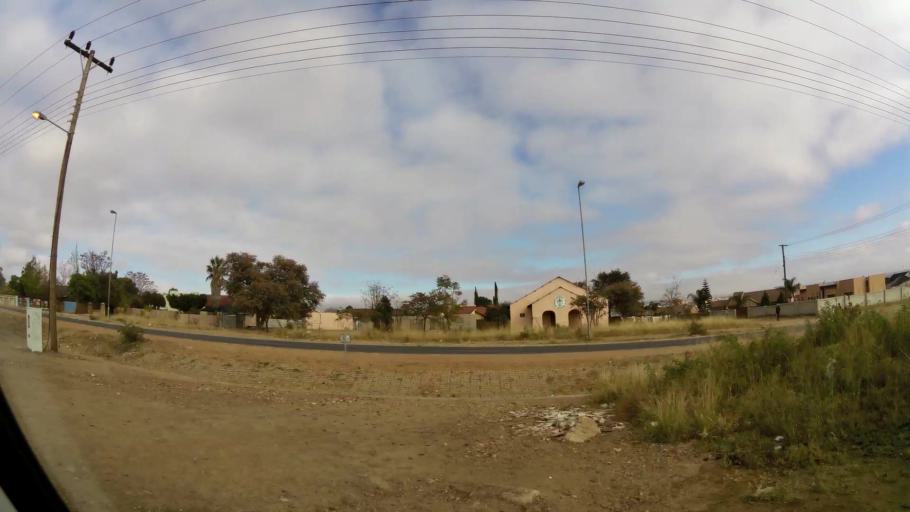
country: ZA
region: Limpopo
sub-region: Capricorn District Municipality
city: Polokwane
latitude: -23.8435
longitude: 29.3793
